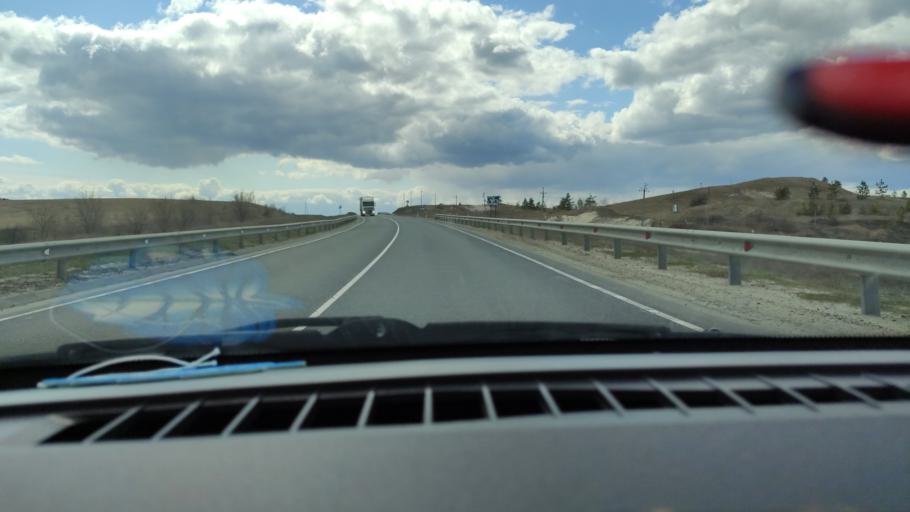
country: RU
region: Saratov
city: Alekseyevka
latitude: 52.3204
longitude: 47.9218
